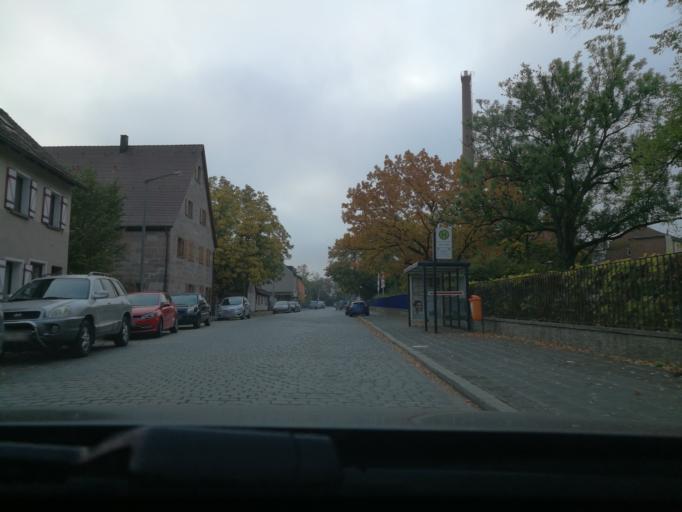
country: DE
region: Bavaria
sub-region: Regierungsbezirk Mittelfranken
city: Wetzendorf
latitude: 49.4967
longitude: 11.0461
